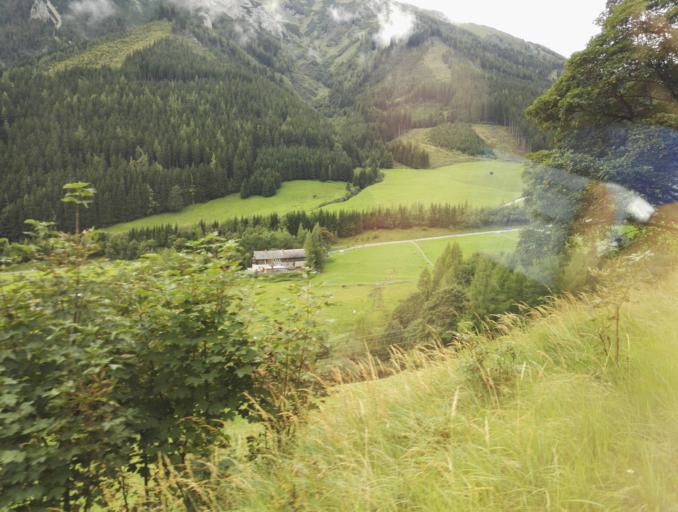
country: AT
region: Styria
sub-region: Politischer Bezirk Leoben
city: Vordernberg
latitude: 47.5039
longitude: 14.9884
